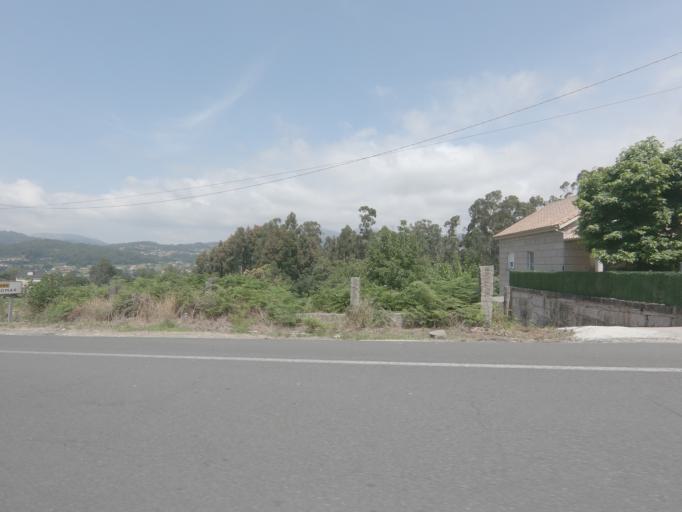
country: ES
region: Galicia
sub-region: Provincia de Pontevedra
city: Gondomar
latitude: 42.0973
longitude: -8.7592
